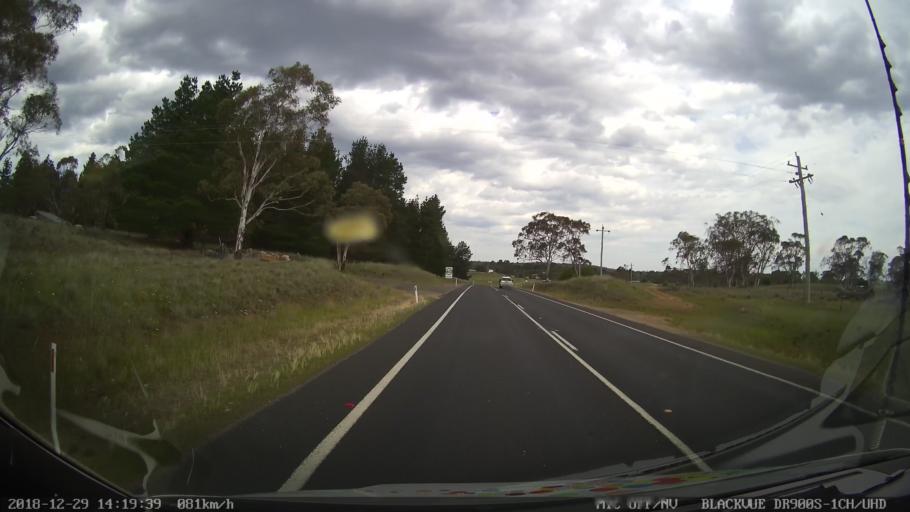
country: AU
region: New South Wales
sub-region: Cooma-Monaro
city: Cooma
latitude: -36.5010
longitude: 149.2826
